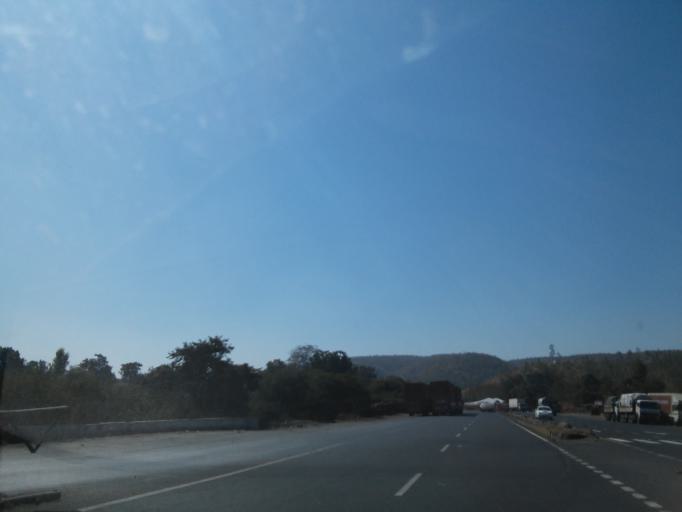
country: IN
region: Gujarat
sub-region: Sabar Kantha
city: Meghraj
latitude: 23.7158
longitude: 73.3931
